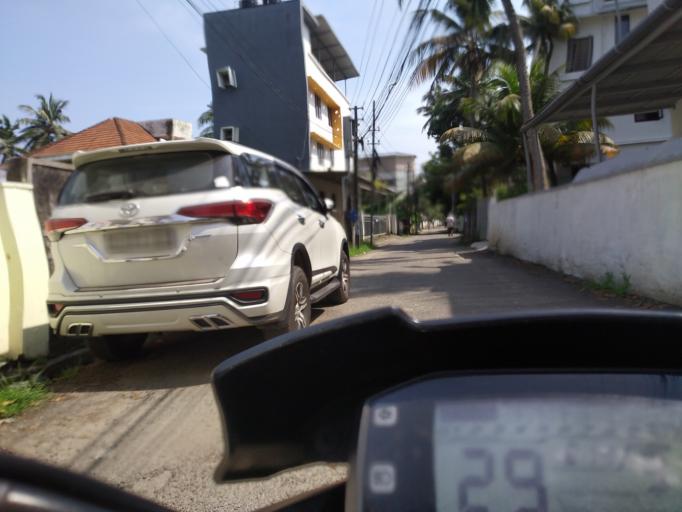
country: IN
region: Kerala
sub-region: Ernakulam
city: Cochin
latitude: 9.9640
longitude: 76.2934
